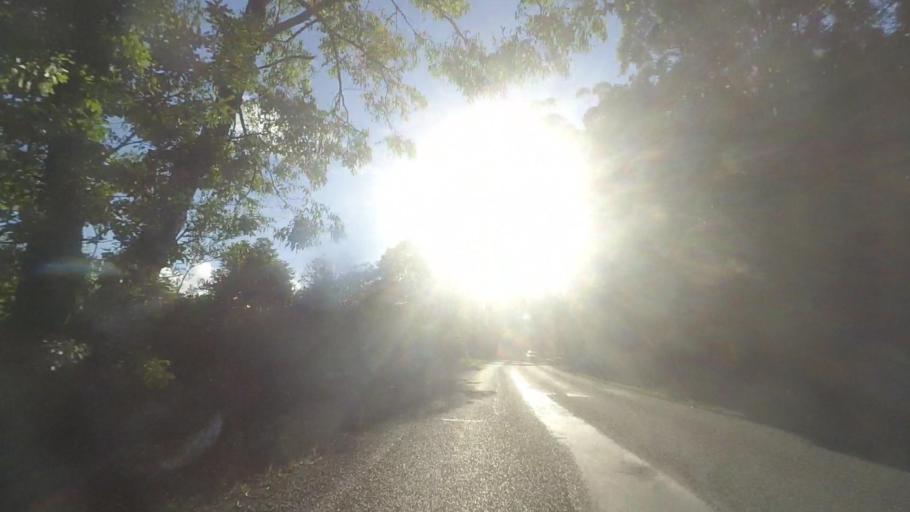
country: AU
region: New South Wales
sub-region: Great Lakes
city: Nabiac
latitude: -32.0915
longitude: 152.4419
